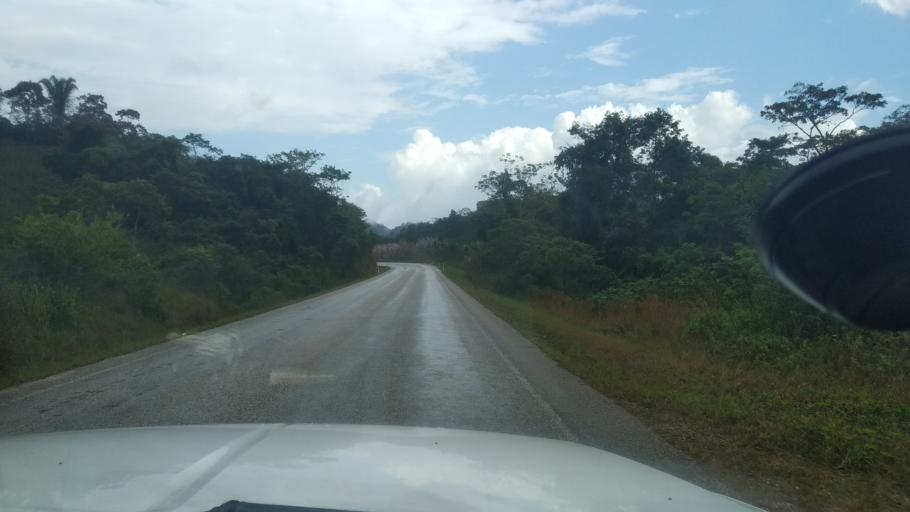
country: GT
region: Peten
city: San Luis
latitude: 16.1891
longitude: -89.1842
